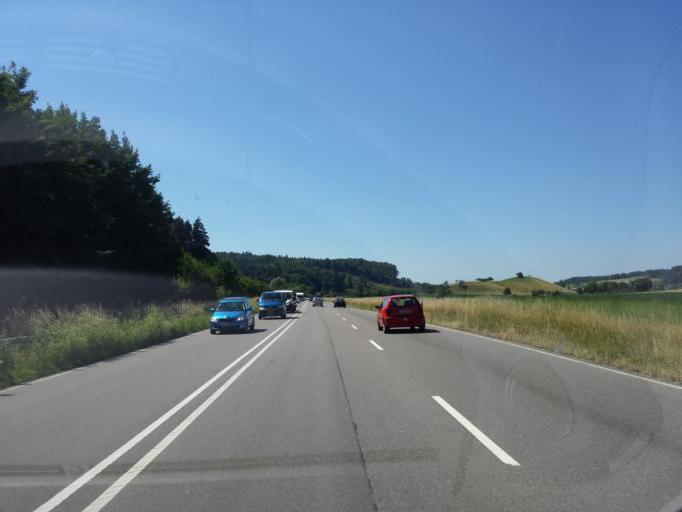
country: DE
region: Baden-Wuerttemberg
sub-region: Tuebingen Region
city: Owingen
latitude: 47.8013
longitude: 9.1321
